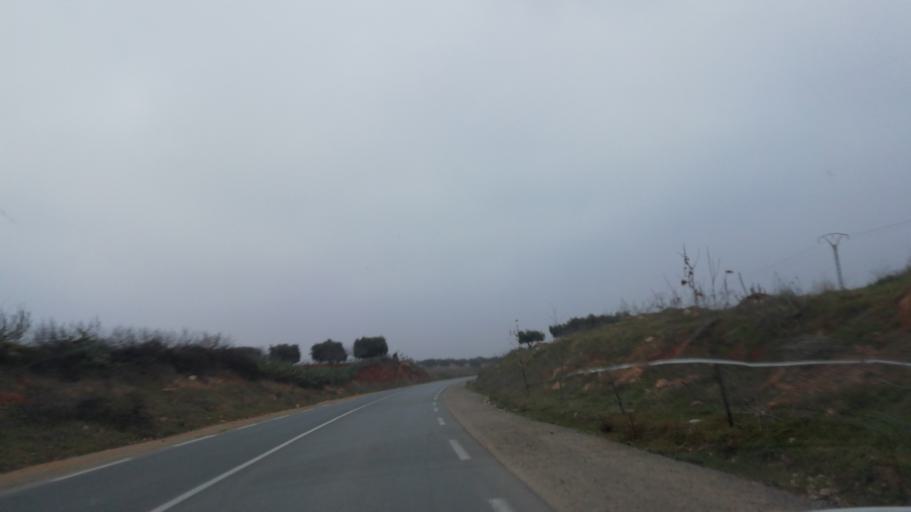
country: DZ
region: Mascara
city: Mascara
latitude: 35.4187
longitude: 0.1221
